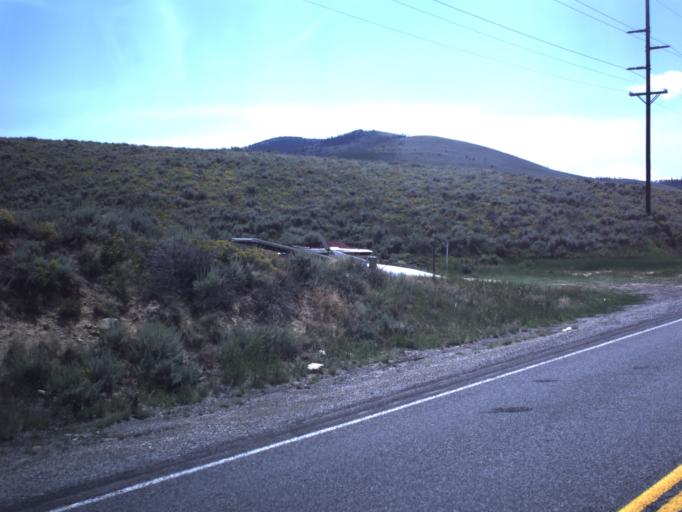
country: US
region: Utah
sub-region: Carbon County
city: Helper
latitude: 39.7937
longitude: -111.1325
